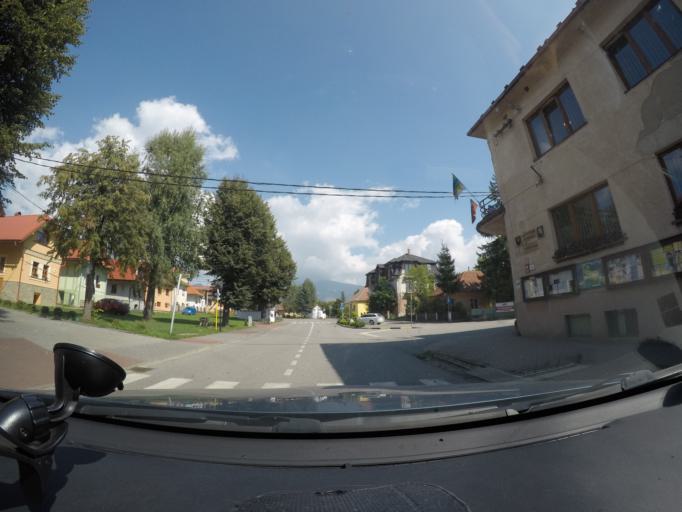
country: SK
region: Zilinsky
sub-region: Okres Liptovsky Mikulas
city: Liptovsky Mikulas
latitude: 49.1192
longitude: 19.6108
